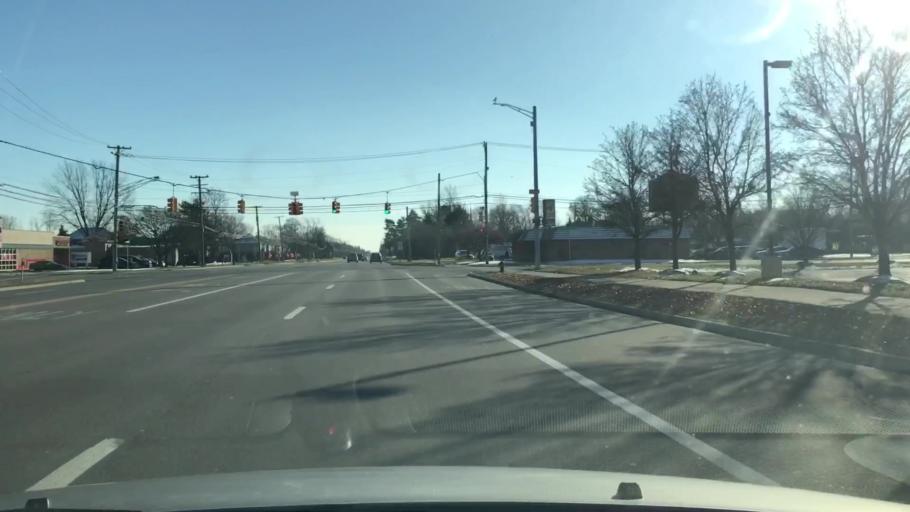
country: US
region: Michigan
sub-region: Oakland County
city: Troy
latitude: 42.5787
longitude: -83.1090
